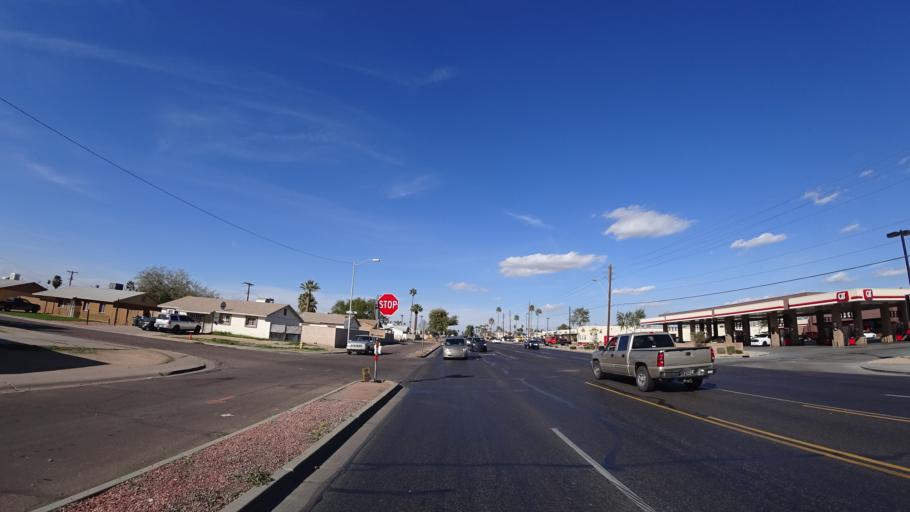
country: US
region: Arizona
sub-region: Maricopa County
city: Tolleson
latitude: 33.4920
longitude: -112.2206
